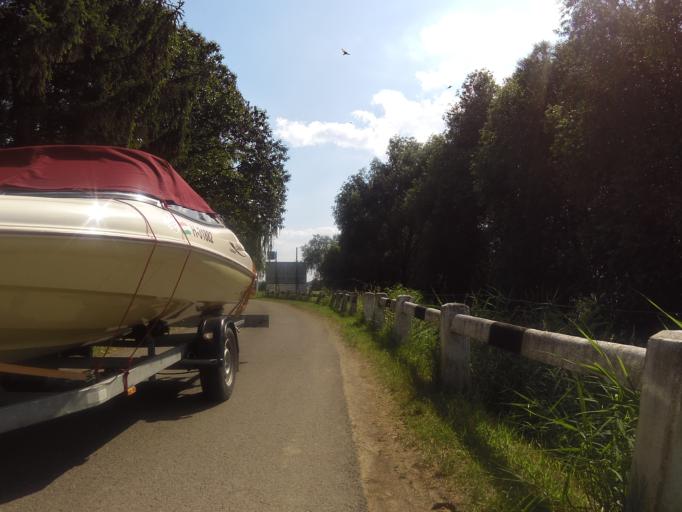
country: HU
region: Jasz-Nagykun-Szolnok
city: Tiszafured
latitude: 47.6072
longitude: 20.7182
